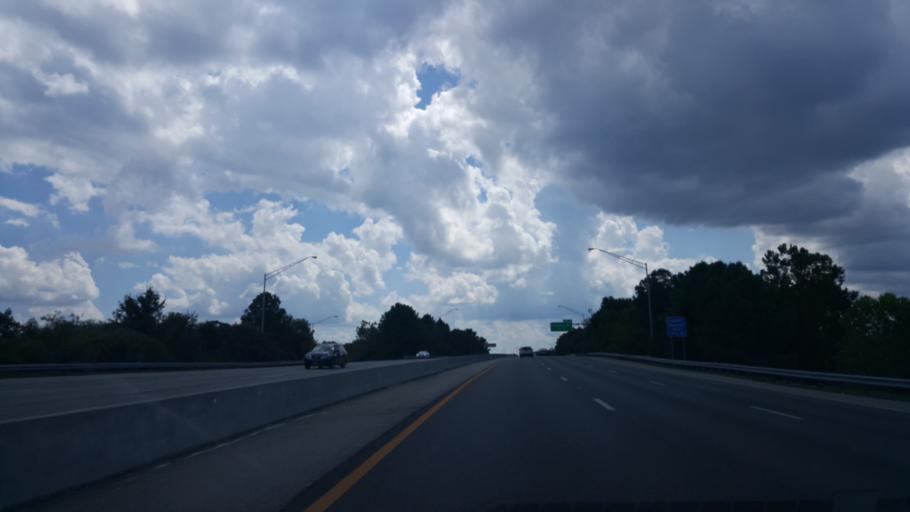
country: US
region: Virginia
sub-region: City of Newport News
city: Newport News
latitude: 37.0056
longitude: -76.4014
